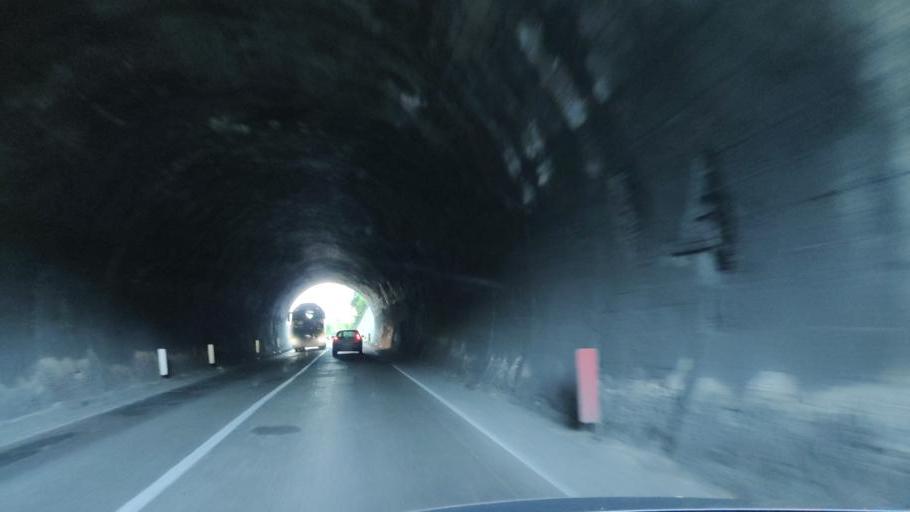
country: IT
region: Umbria
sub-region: Provincia di Terni
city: Narni Scalo
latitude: 42.5264
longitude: 12.5134
